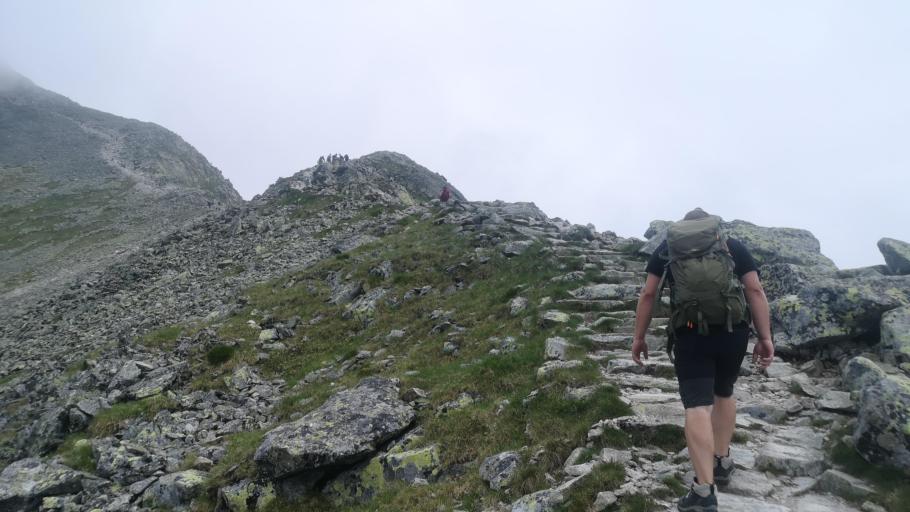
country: SK
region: Presovsky
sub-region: Okres Poprad
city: Strba
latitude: 49.1579
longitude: 20.0005
